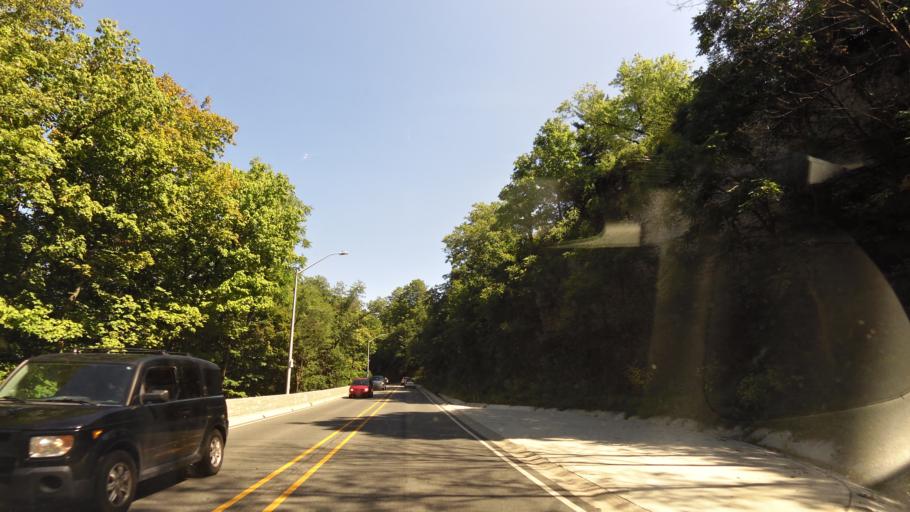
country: CA
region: Ontario
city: Hamilton
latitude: 43.2444
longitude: -79.8932
